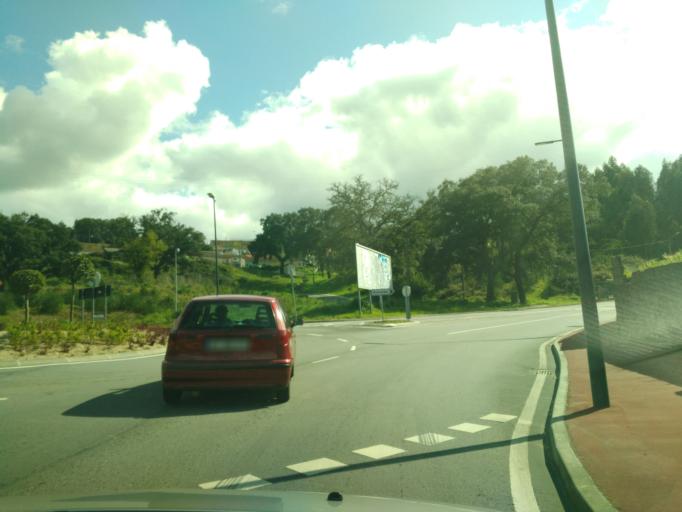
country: PT
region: Braga
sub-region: Braga
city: Braga
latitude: 41.5388
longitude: -8.4185
